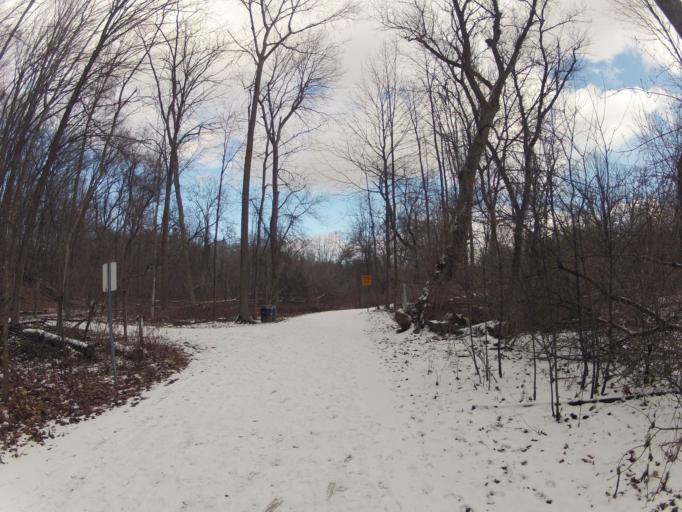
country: CA
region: Ontario
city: Mississauga
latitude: 43.5634
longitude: -79.6791
